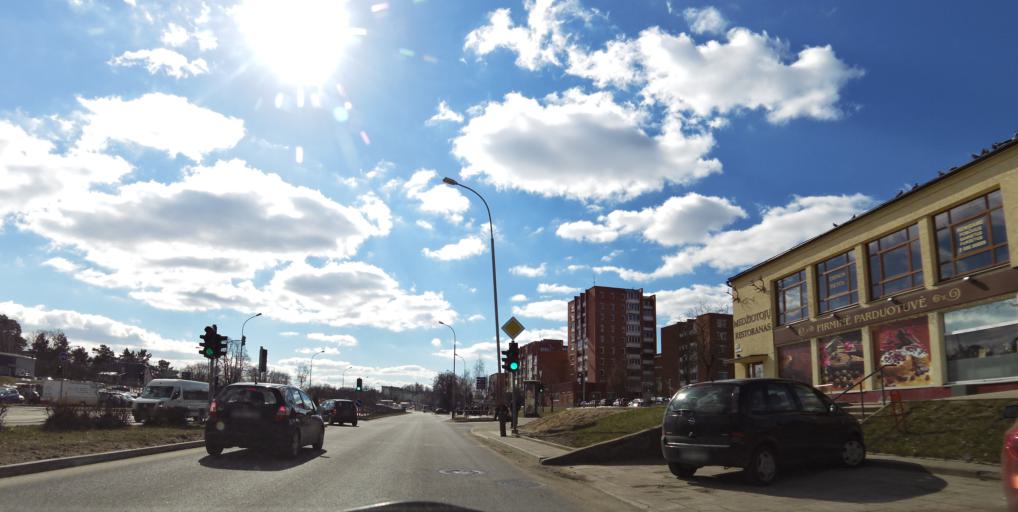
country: LT
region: Vilnius County
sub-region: Vilnius
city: Fabijoniskes
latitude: 54.7440
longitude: 25.2775
